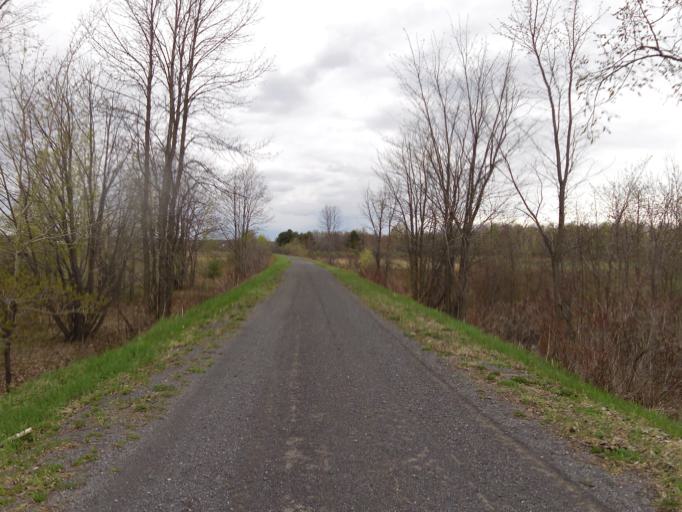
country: CA
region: Quebec
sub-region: Outaouais
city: Papineauville
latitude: 45.5196
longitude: -74.9682
